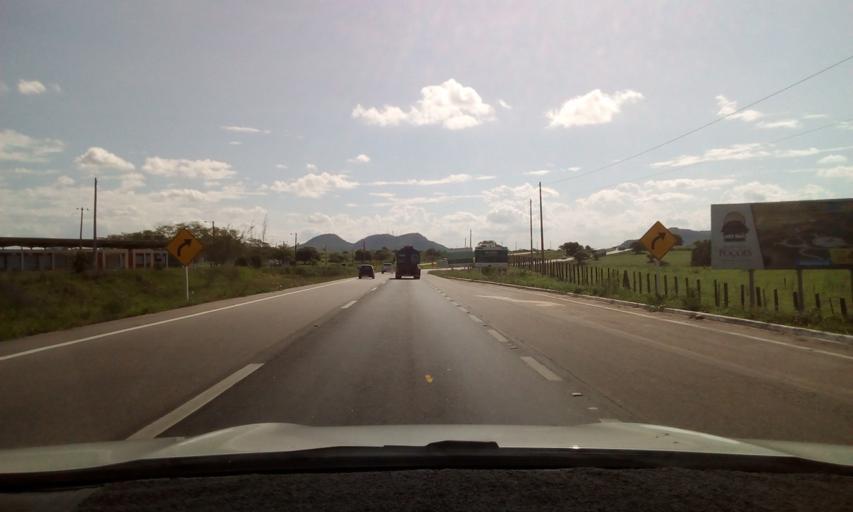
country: BR
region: Paraiba
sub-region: Gurinhem
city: Gurinhem
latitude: -7.1659
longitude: -35.3551
